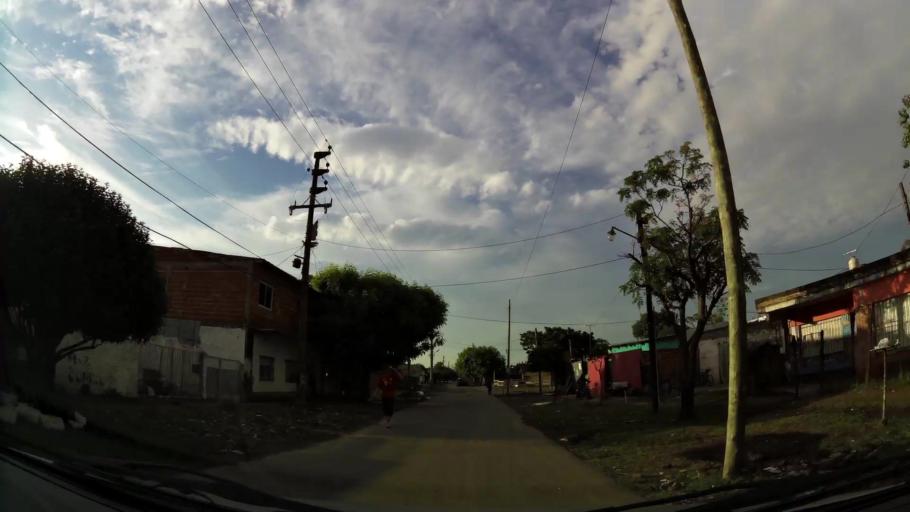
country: AR
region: Buenos Aires
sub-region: Partido de Lomas de Zamora
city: Lomas de Zamora
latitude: -34.7572
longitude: -58.3605
